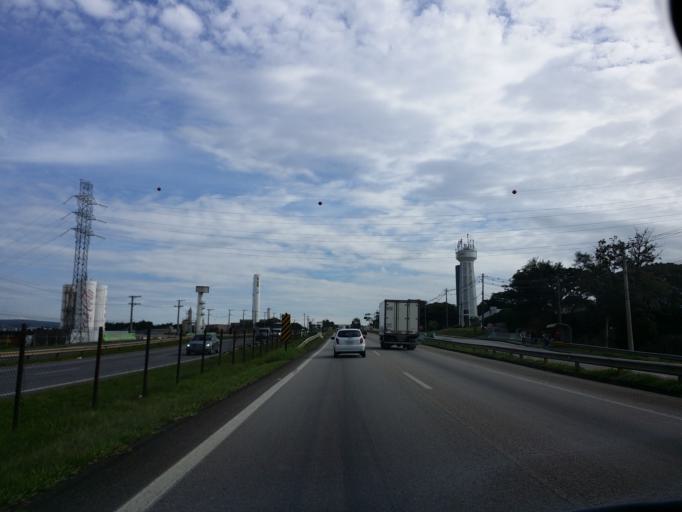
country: BR
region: Sao Paulo
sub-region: Jundiai
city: Jundiai
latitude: -23.1760
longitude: -46.9538
